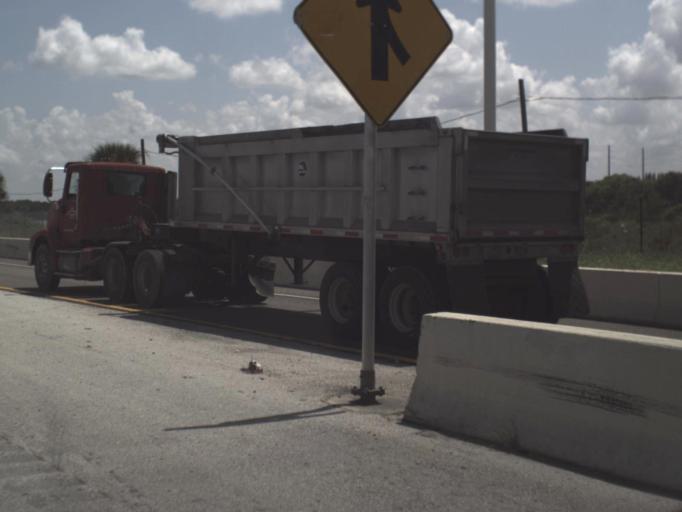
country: US
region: Florida
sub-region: Hillsborough County
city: East Lake-Orient Park
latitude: 27.9711
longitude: -82.3973
